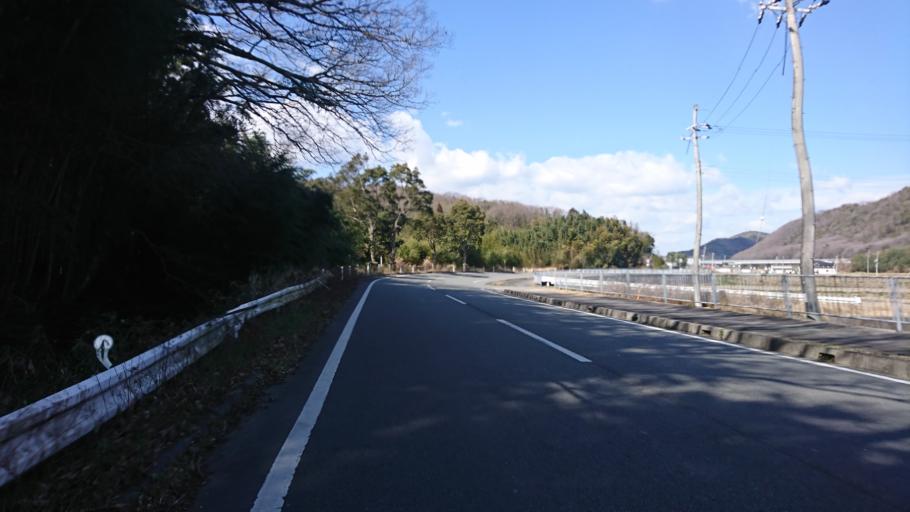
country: JP
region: Hyogo
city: Kakogawacho-honmachi
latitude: 34.8424
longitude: 134.8166
